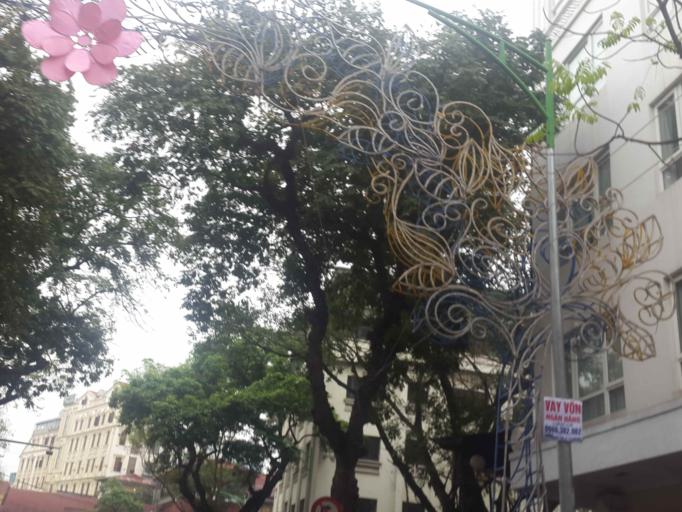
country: VN
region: Ha Noi
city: Hoan Kiem
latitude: 21.0398
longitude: 105.8463
